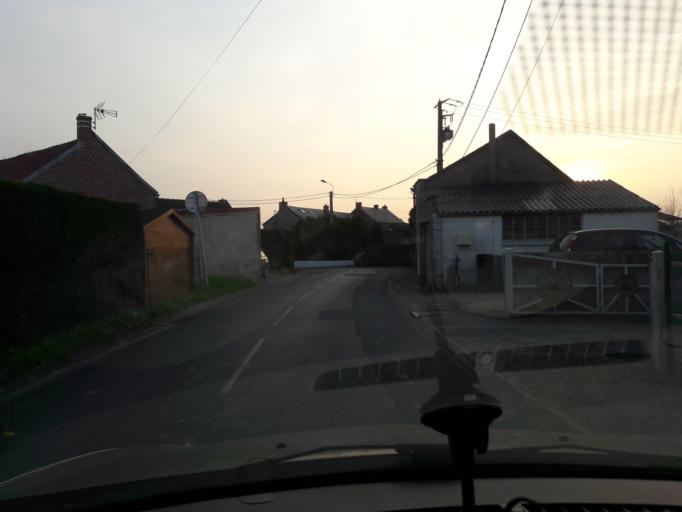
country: FR
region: Nord-Pas-de-Calais
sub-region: Departement du Nord
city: Recquignies
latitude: 50.2625
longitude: 4.0280
